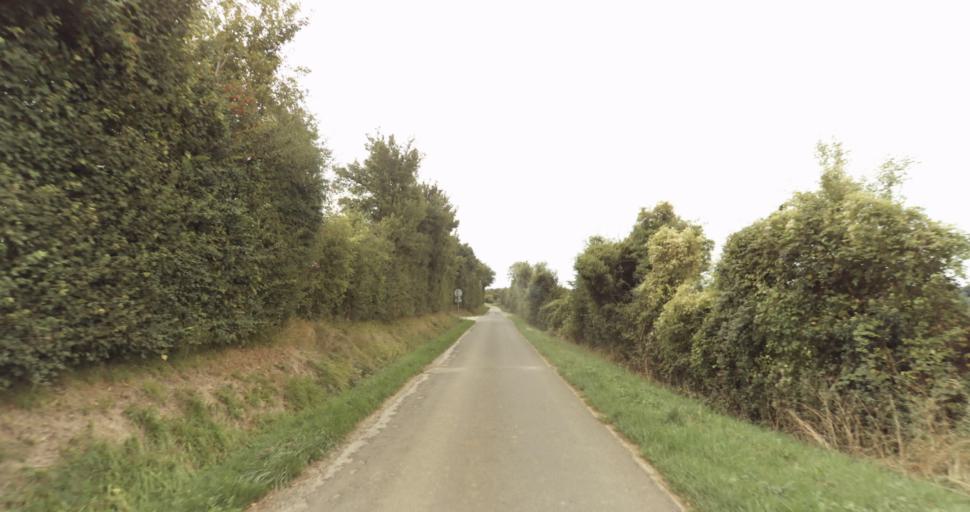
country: FR
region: Lower Normandy
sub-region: Departement de l'Orne
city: Gace
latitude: 48.7620
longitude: 0.3431
